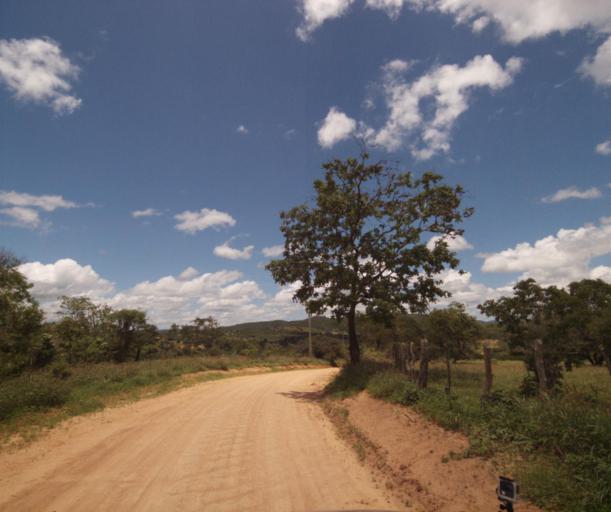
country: BR
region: Bahia
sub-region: Pocoes
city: Pocoes
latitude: -14.3820
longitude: -40.3667
